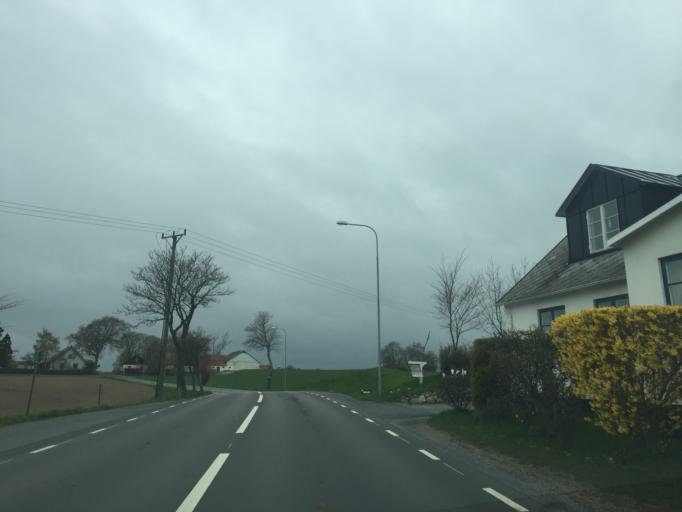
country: SE
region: Skane
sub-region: Skurups Kommun
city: Skivarp
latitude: 55.4230
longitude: 13.6216
